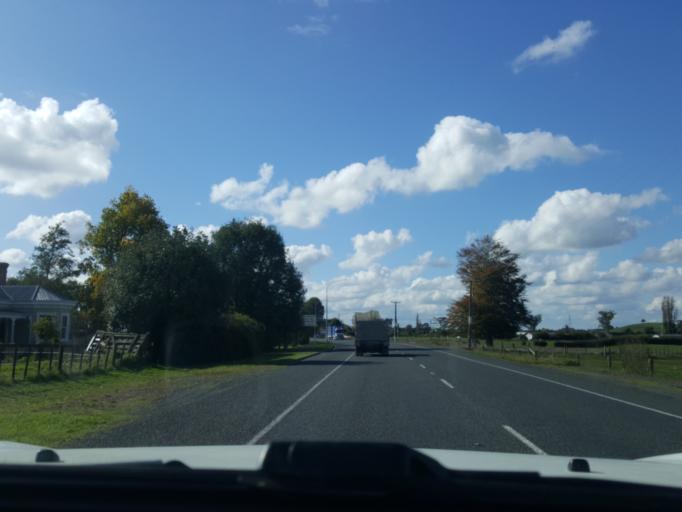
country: NZ
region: Waikato
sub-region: Waikato District
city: Ngaruawahia
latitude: -37.6270
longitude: 175.1819
